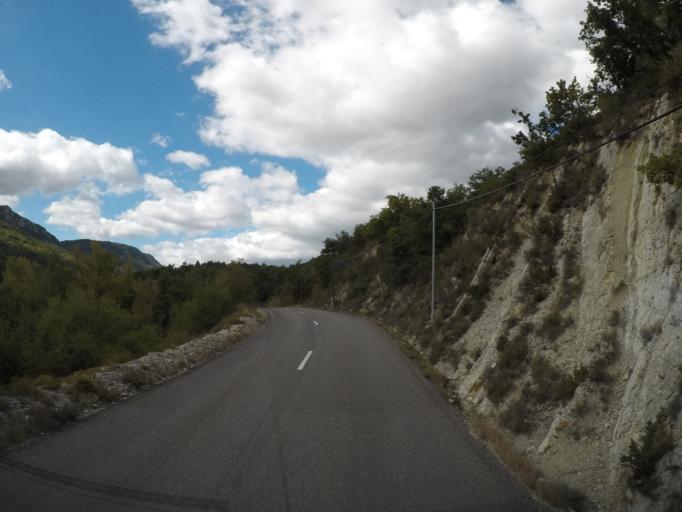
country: FR
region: Provence-Alpes-Cote d'Azur
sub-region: Departement des Hautes-Alpes
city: Laragne-Monteglin
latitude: 44.1750
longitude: 5.7021
